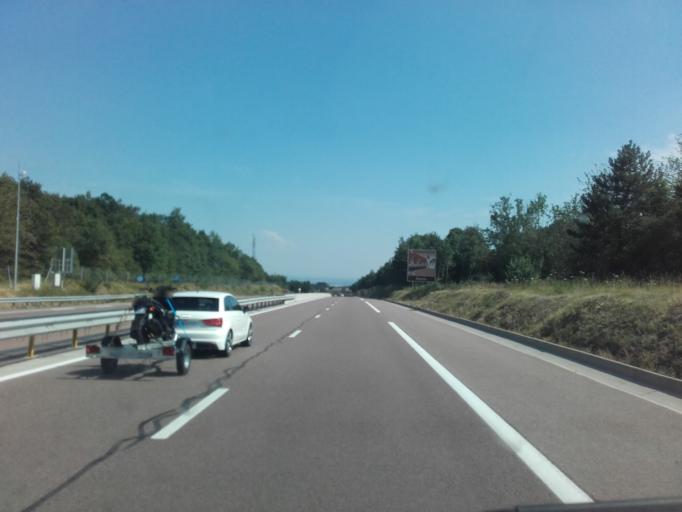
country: FR
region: Bourgogne
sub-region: Departement de la Cote-d'Or
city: Savigny-les-Beaune
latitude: 47.0659
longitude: 4.7680
